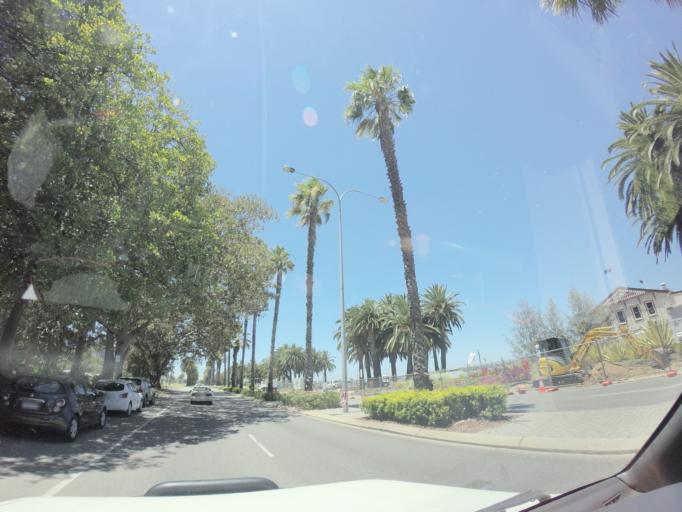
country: AU
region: Western Australia
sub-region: Cambridge
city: Perth
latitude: -31.9591
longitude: 115.8600
